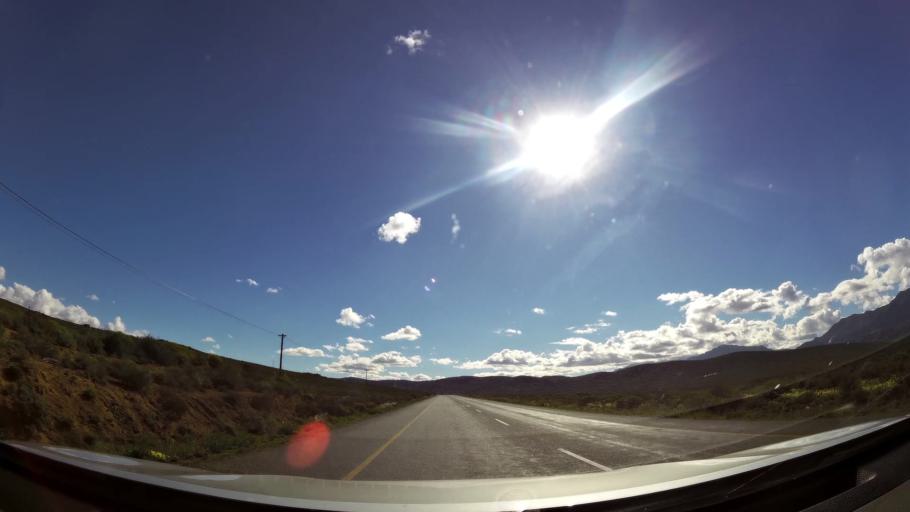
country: ZA
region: Western Cape
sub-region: Cape Winelands District Municipality
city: Worcester
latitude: -33.7455
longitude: 19.7004
